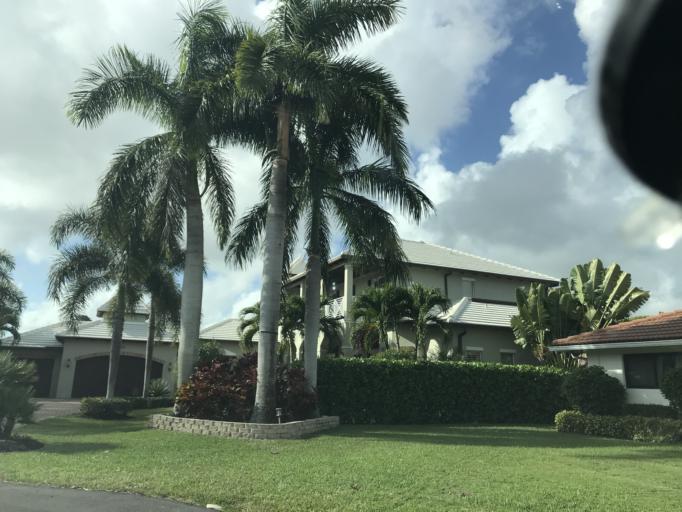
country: US
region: Florida
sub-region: Palm Beach County
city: Delray Beach
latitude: 26.4743
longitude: -80.0851
